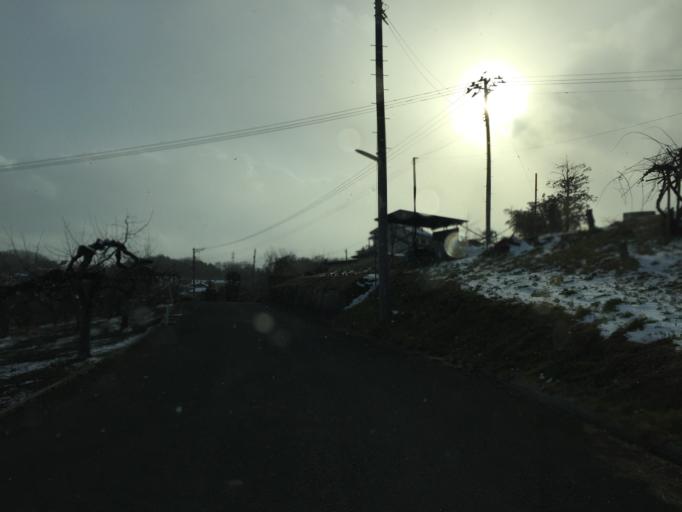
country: JP
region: Fukushima
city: Fukushima-shi
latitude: 37.8402
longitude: 140.4594
